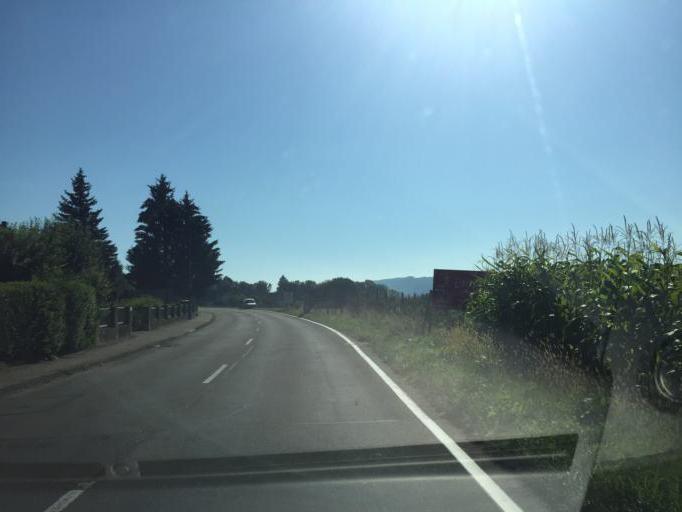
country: DE
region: Baden-Wuerttemberg
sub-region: Freiburg Region
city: Ohningen
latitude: 47.6602
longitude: 8.8776
